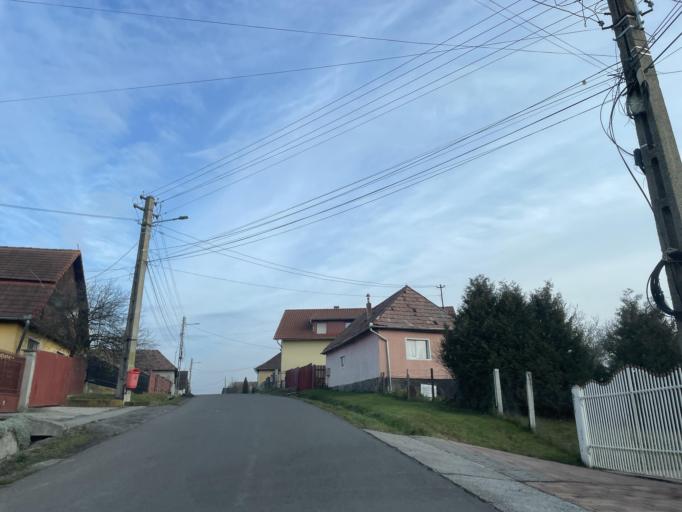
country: RO
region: Mures
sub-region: Comuna Solovastru
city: Solovastru
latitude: 46.7756
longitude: 24.7582
